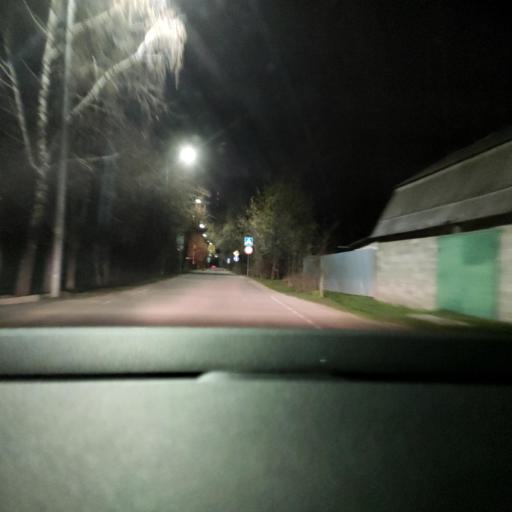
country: RU
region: Moskovskaya
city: Reutov
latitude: 55.7666
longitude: 37.8878
